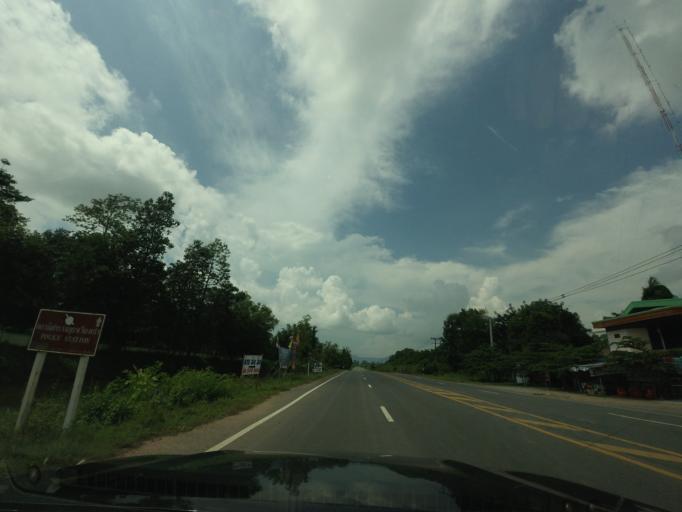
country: TH
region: Khon Kaen
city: Wiang Kao
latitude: 16.6752
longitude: 102.3259
